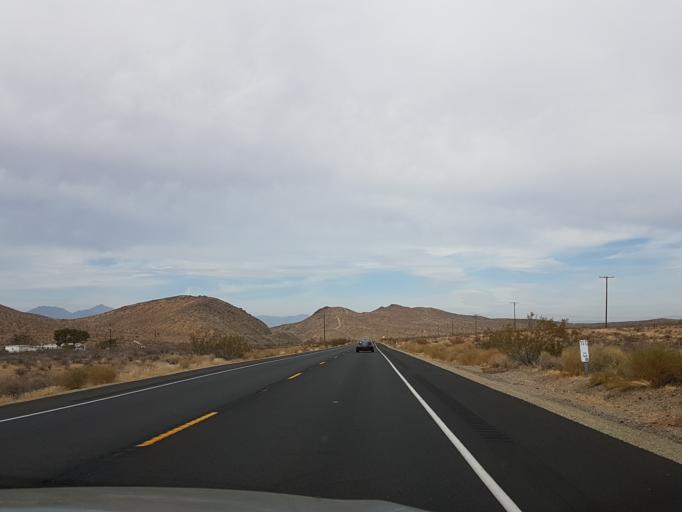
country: US
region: California
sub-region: Kern County
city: Ridgecrest
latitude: 35.5363
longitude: -117.6839
